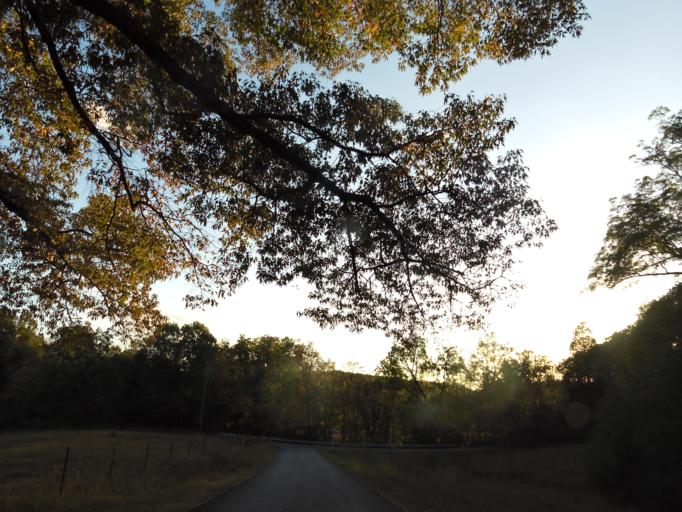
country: US
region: Tennessee
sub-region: Sevier County
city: Seymour
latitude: 35.9560
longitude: -83.7280
